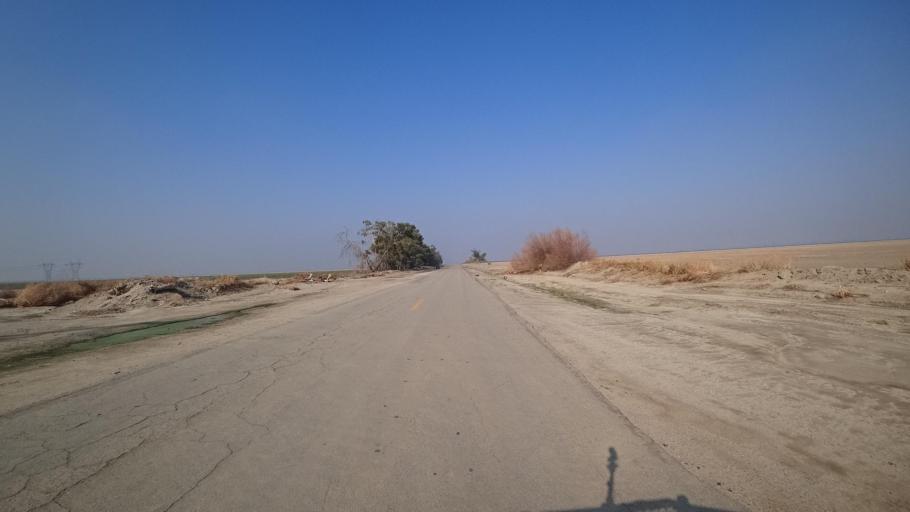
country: US
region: California
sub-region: Kern County
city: Greenfield
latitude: 35.1586
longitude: -119.0393
